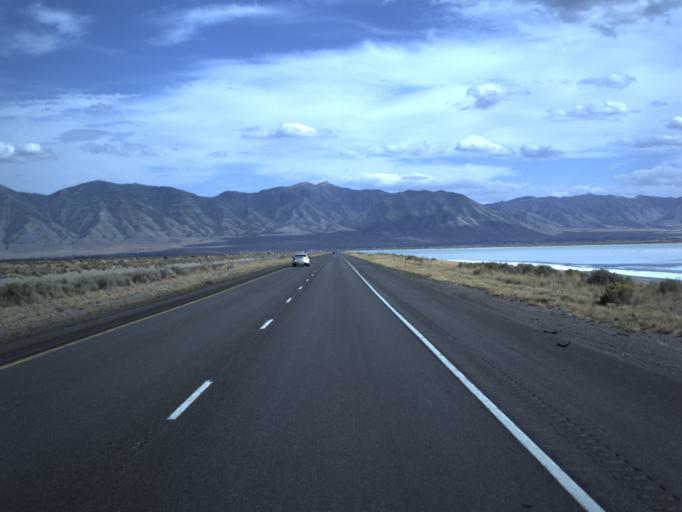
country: US
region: Utah
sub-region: Tooele County
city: Grantsville
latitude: 40.6780
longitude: -112.4116
